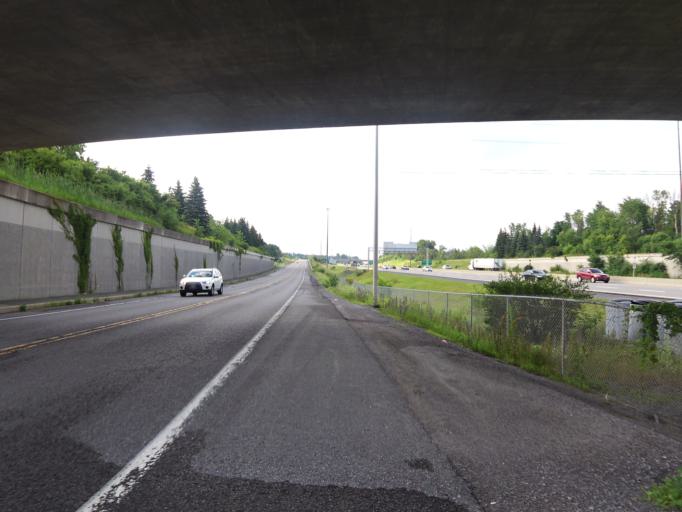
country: CA
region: Ontario
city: Bells Corners
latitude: 45.3316
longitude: -75.8089
